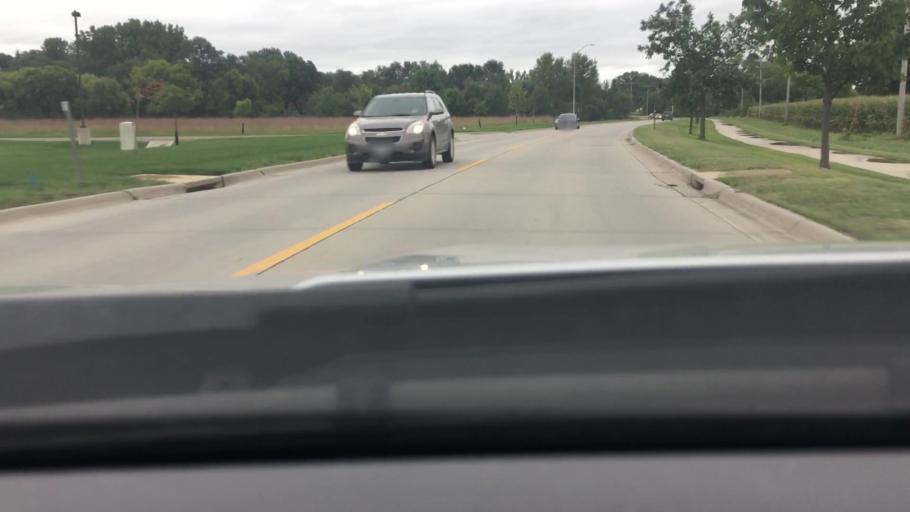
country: US
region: Iowa
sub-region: Pottawattamie County
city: Council Bluffs
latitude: 41.2639
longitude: -95.8042
